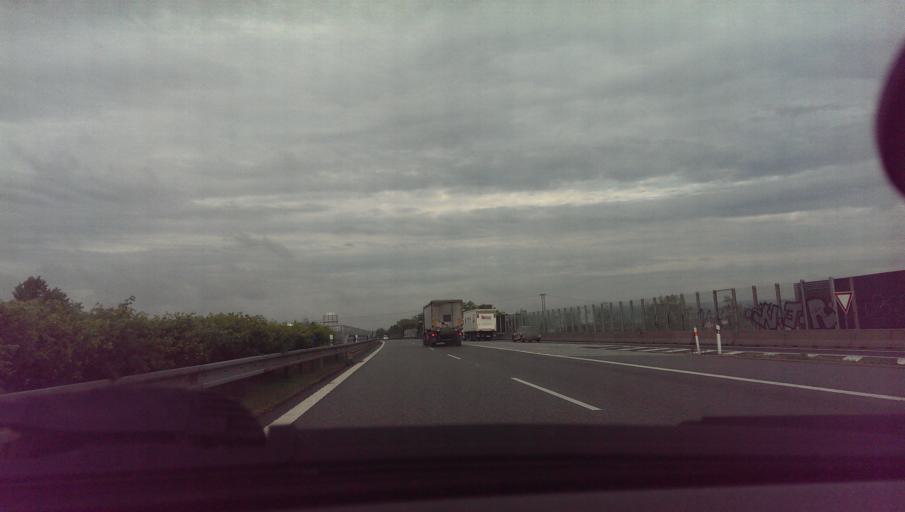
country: CZ
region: South Moravian
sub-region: Okres Vyskov
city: Vyskov
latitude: 49.2707
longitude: 17.0166
